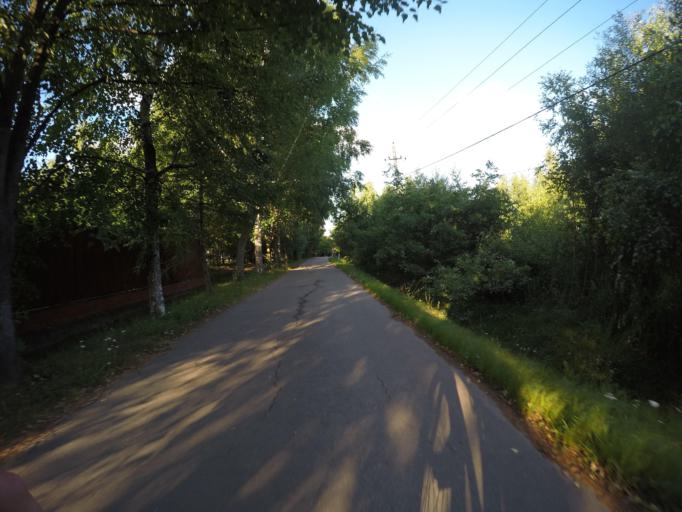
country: RU
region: Moskovskaya
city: Rechitsy
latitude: 55.5957
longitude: 38.4949
